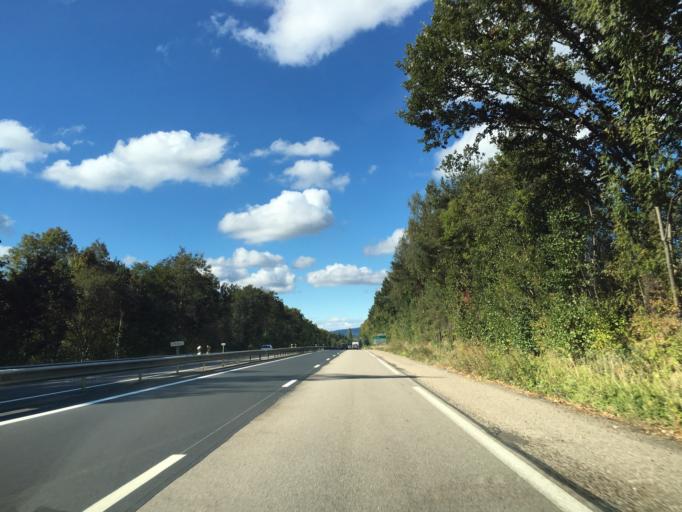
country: FR
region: Lorraine
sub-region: Departement des Vosges
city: Saint-Michel-sur-Meurthe
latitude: 48.3205
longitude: 6.9138
